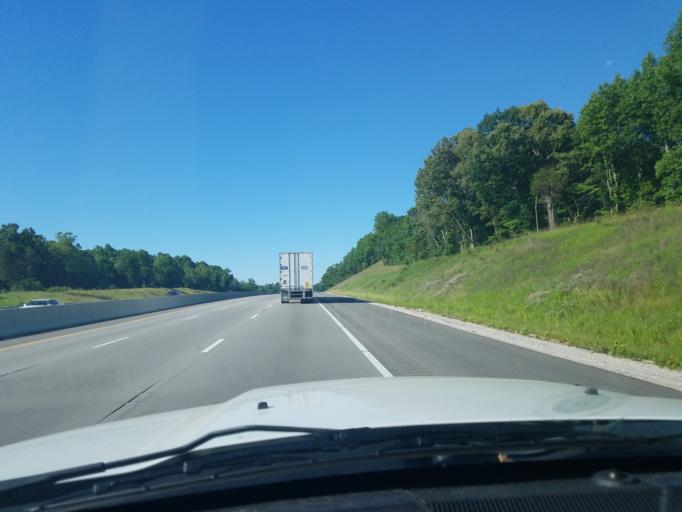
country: US
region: Kentucky
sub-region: Hart County
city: Munfordville
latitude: 37.3725
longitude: -85.8911
